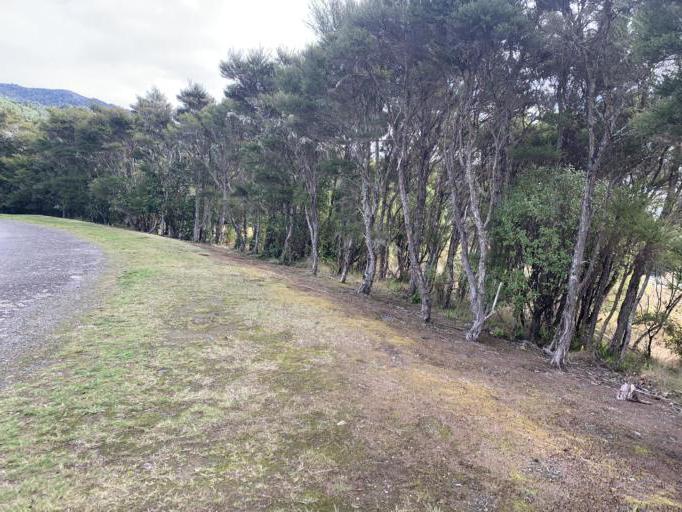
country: NZ
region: Waikato
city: Turangi
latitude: -38.9804
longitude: 175.7730
